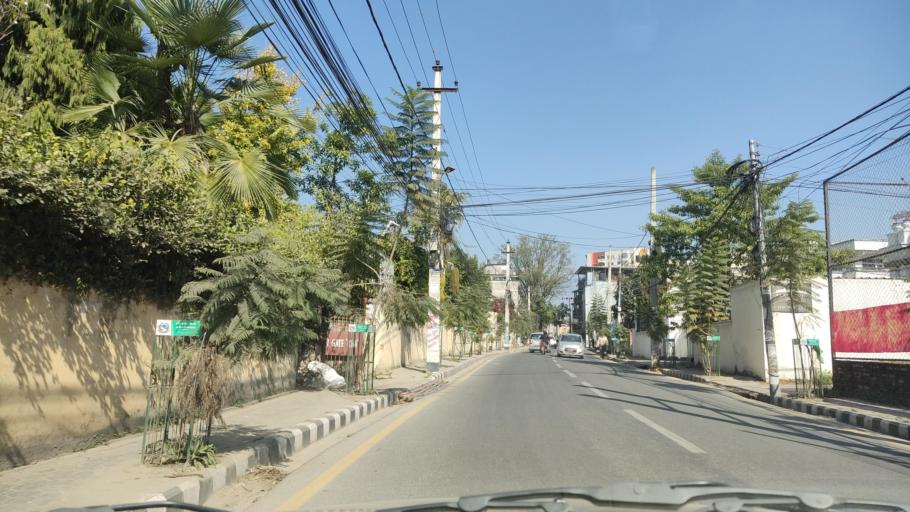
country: NP
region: Central Region
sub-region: Bagmati Zone
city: Kathmandu
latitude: 27.7208
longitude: 85.3348
